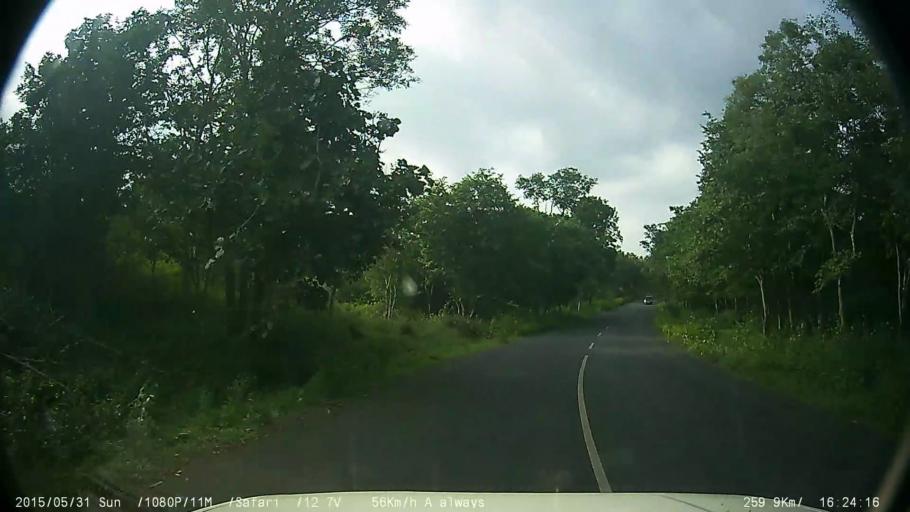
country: IN
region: Karnataka
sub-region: Chamrajnagar
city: Gundlupet
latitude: 11.7624
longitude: 76.5213
